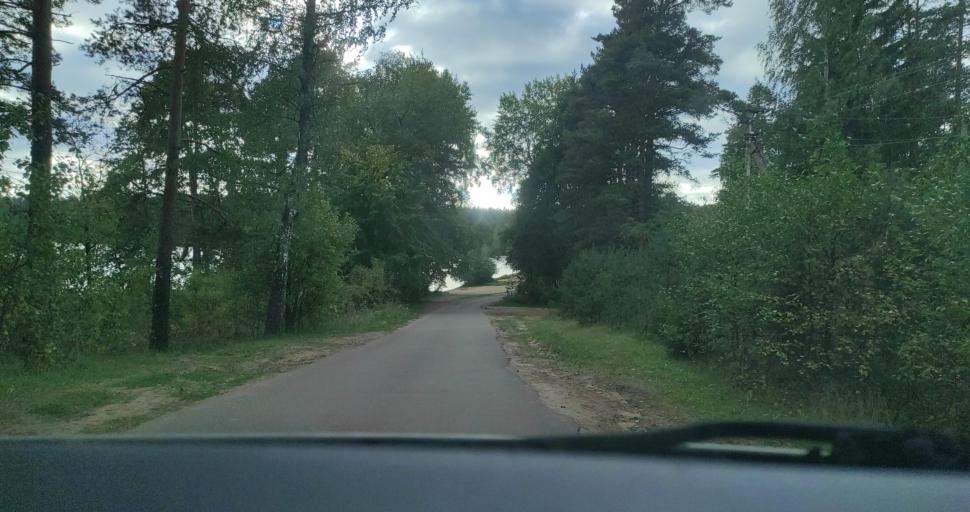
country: RU
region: Leningrad
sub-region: Vsevolzhskij Rajon
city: Vaskelovo
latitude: 60.4030
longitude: 30.3153
